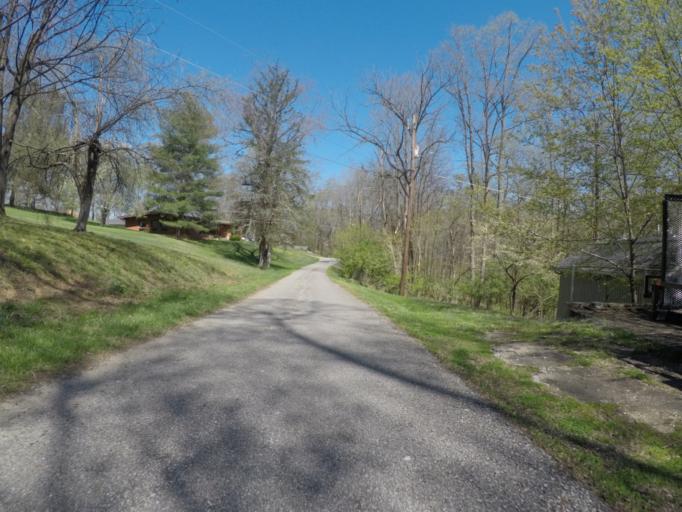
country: US
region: West Virginia
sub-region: Cabell County
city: Pea Ridge
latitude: 38.4141
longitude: -82.3182
